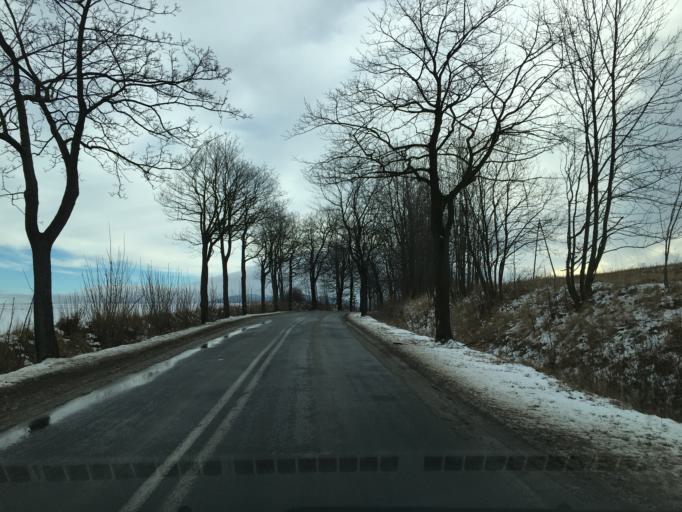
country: PL
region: Lower Silesian Voivodeship
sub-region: Powiat walbrzyski
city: Jedlina-Zdroj
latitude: 50.7377
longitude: 16.3470
